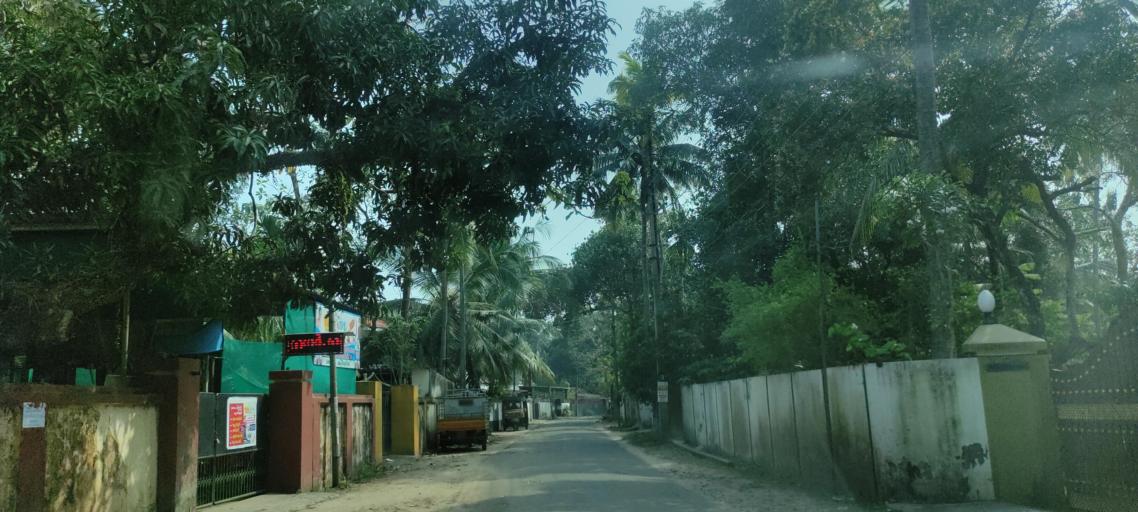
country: IN
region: Kerala
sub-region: Alappuzha
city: Shertallai
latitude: 9.6827
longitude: 76.3367
